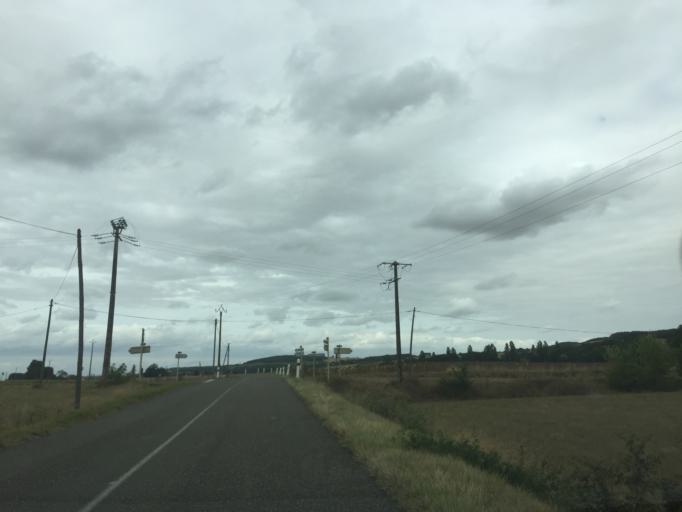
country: FR
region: Midi-Pyrenees
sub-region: Departement du Gers
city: Vic-Fezensac
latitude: 43.7854
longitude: 0.3868
